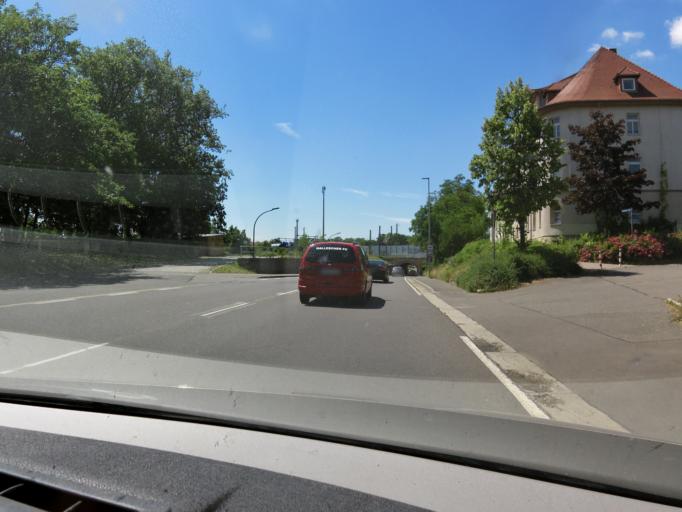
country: DE
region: Saxony-Anhalt
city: Merseburg
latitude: 51.3503
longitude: 11.9920
